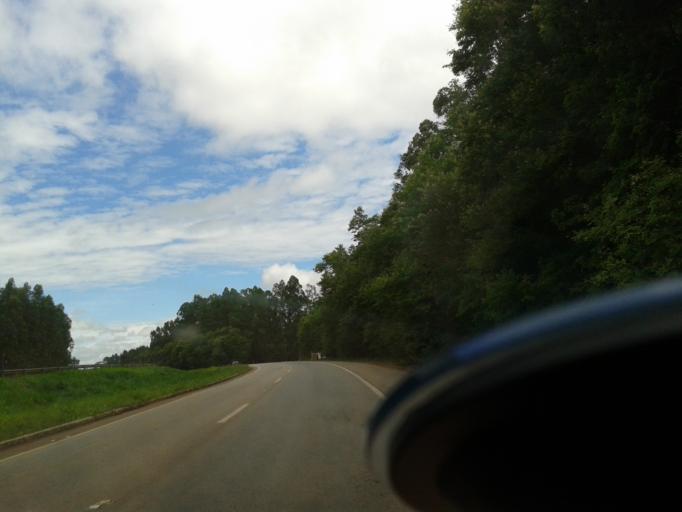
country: BR
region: Goias
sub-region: Inhumas
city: Inhumas
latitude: -16.3296
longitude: -49.5182
